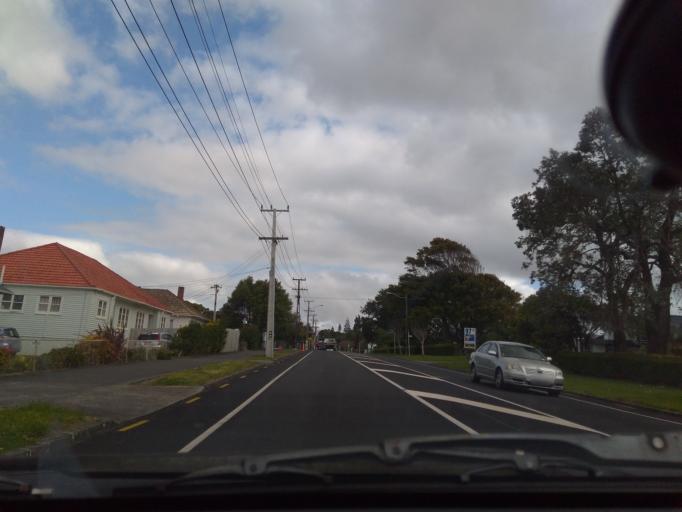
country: NZ
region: Auckland
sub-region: Auckland
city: Rosebank
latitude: -36.8763
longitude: 174.7106
